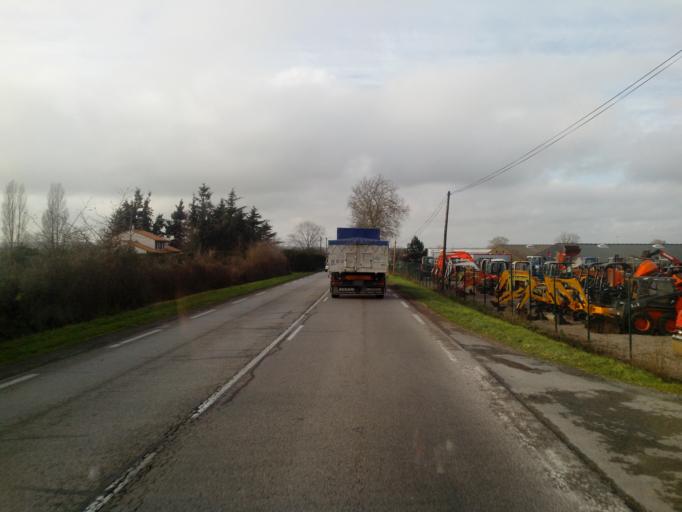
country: FR
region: Poitou-Charentes
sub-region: Departement des Deux-Sevres
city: Chiche
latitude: 46.7916
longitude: -0.3464
